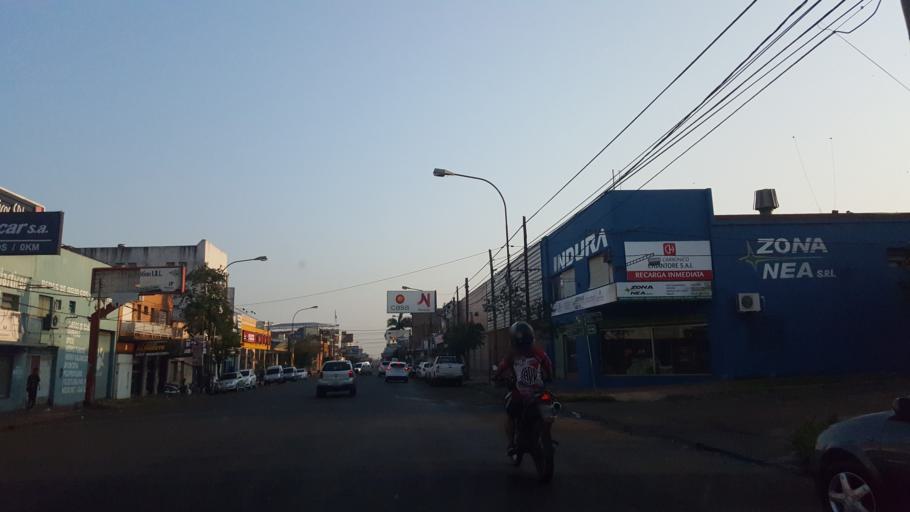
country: AR
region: Misiones
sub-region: Departamento de Capital
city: Posadas
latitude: -27.3899
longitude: -55.9007
